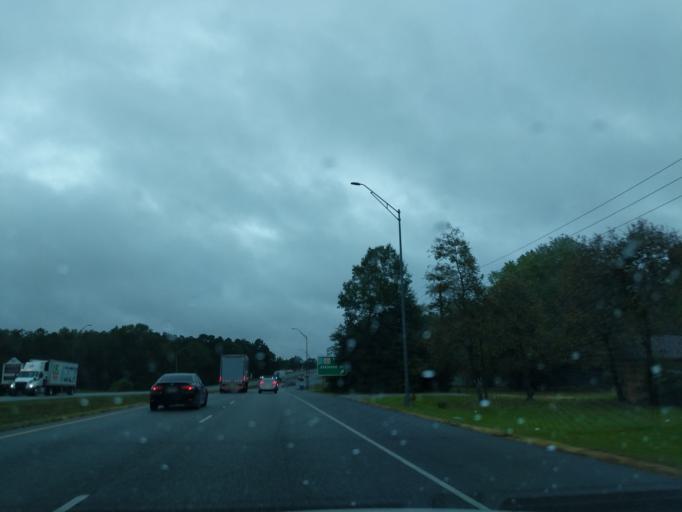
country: US
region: Texas
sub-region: Angelina County
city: Lufkin
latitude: 31.3474
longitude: -94.6943
